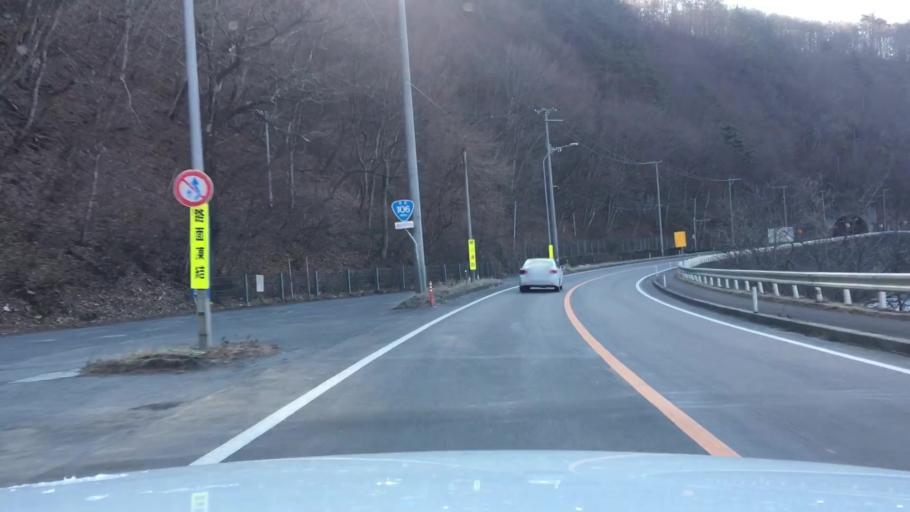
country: JP
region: Iwate
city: Tono
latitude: 39.6404
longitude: 141.6001
